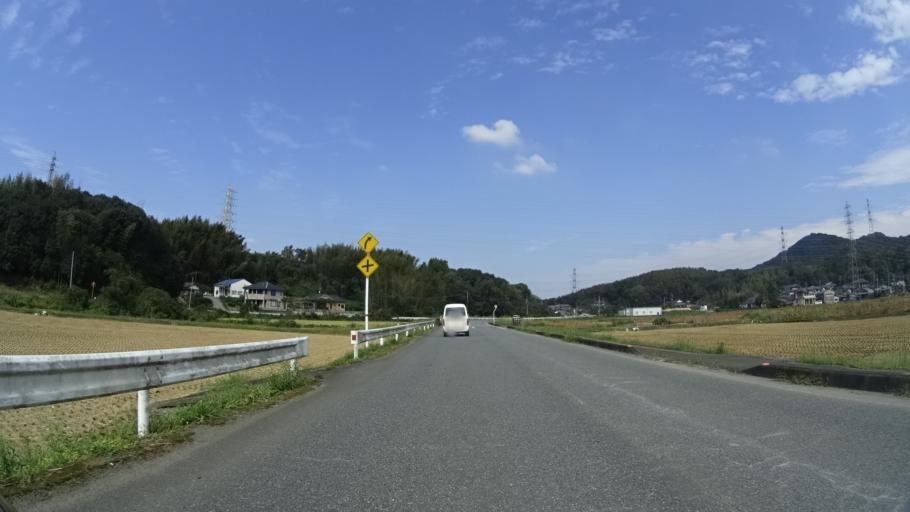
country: JP
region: Kumamoto
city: Matsubase
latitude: 32.6544
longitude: 130.7159
